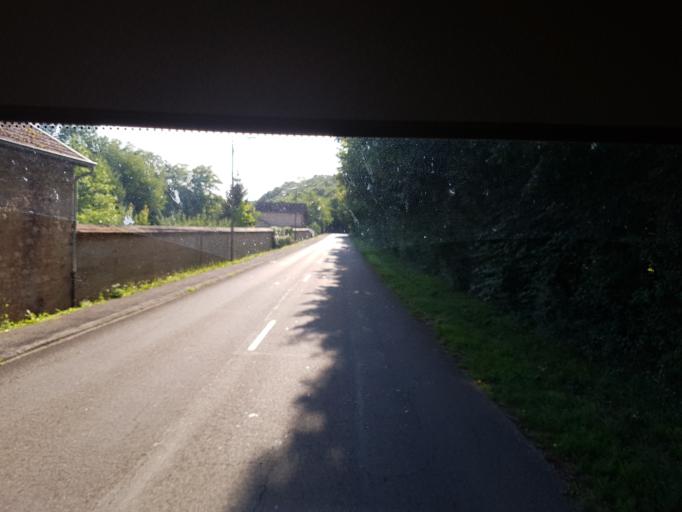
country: FR
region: Rhone-Alpes
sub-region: Departement de l'Ain
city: Neuville-sur-Ain
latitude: 46.0552
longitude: 5.3555
